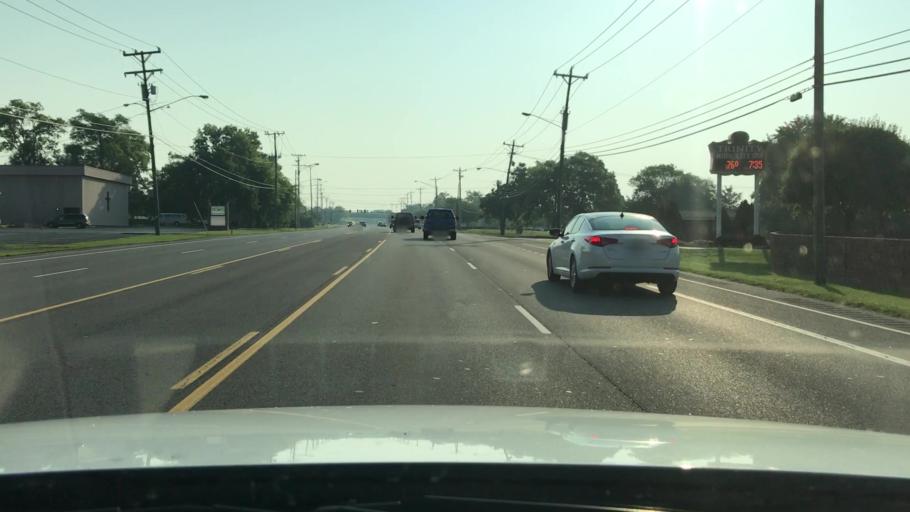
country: US
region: Tennessee
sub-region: Sumner County
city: Hendersonville
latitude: 36.3251
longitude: -86.5656
